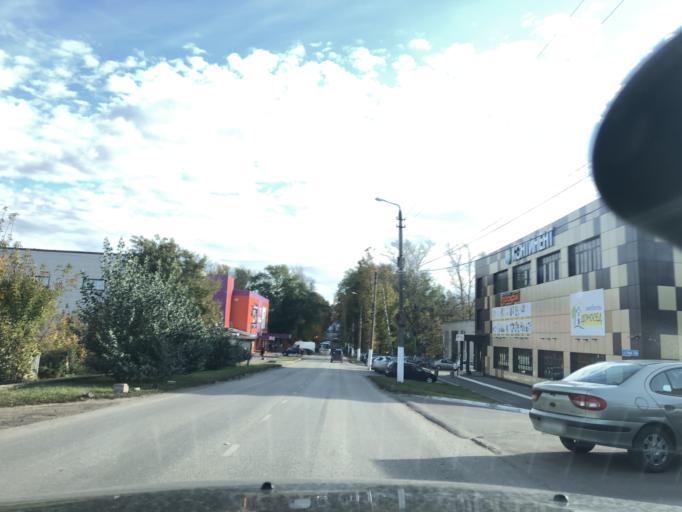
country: RU
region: Tula
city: Kireyevsk
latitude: 53.9306
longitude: 37.9274
